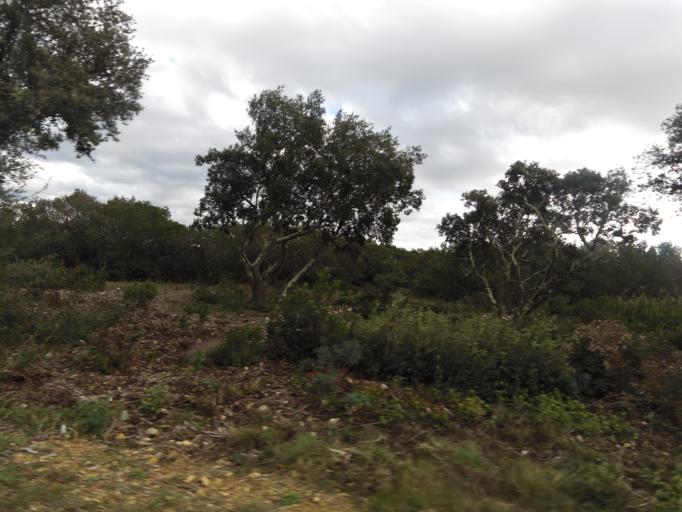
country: FR
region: Languedoc-Roussillon
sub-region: Departement du Gard
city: Clarensac
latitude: 43.8388
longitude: 4.1908
